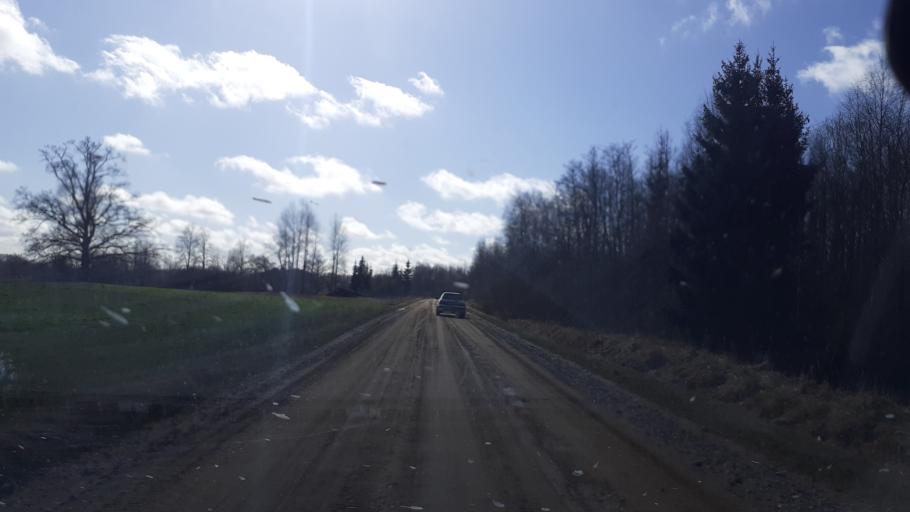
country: LV
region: Kuldigas Rajons
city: Kuldiga
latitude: 56.9209
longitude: 22.1324
